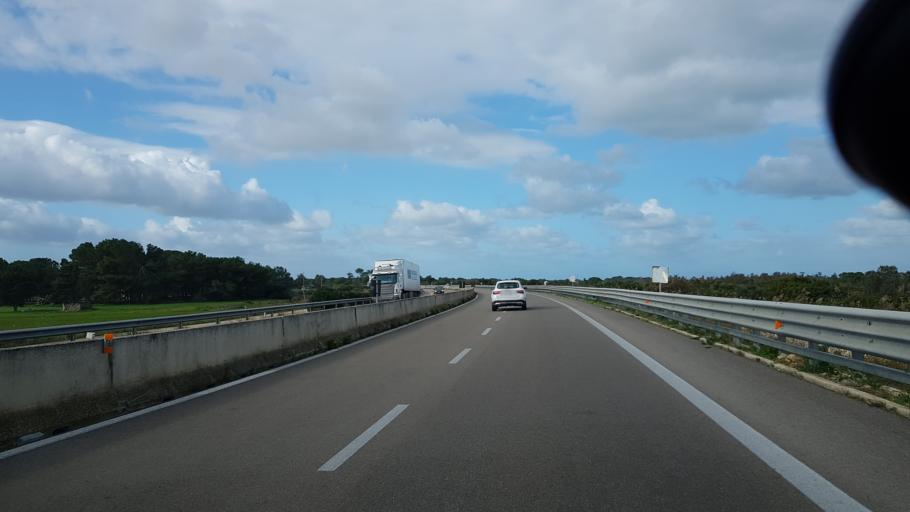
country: IT
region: Apulia
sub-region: Provincia di Brindisi
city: San Vito dei Normanni
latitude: 40.7125
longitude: 17.7864
